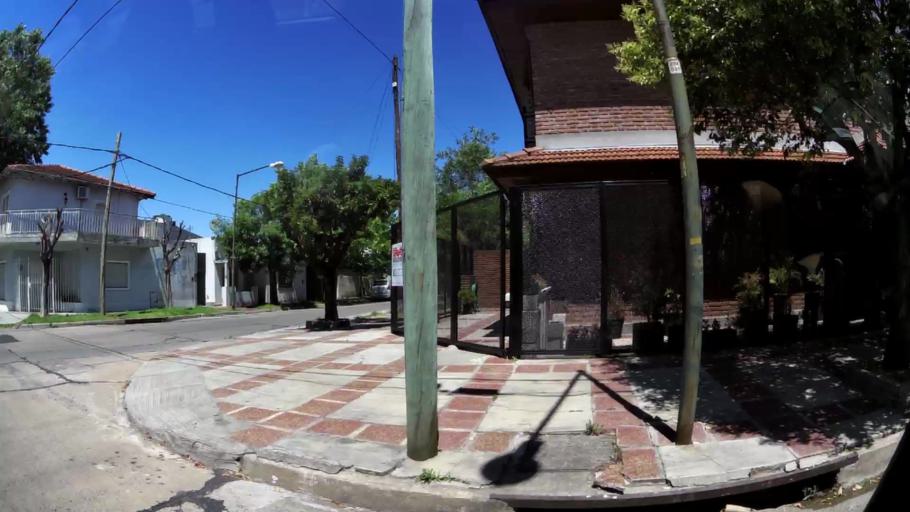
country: AR
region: Buenos Aires
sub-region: Partido de San Isidro
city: San Isidro
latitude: -34.5008
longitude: -58.5311
